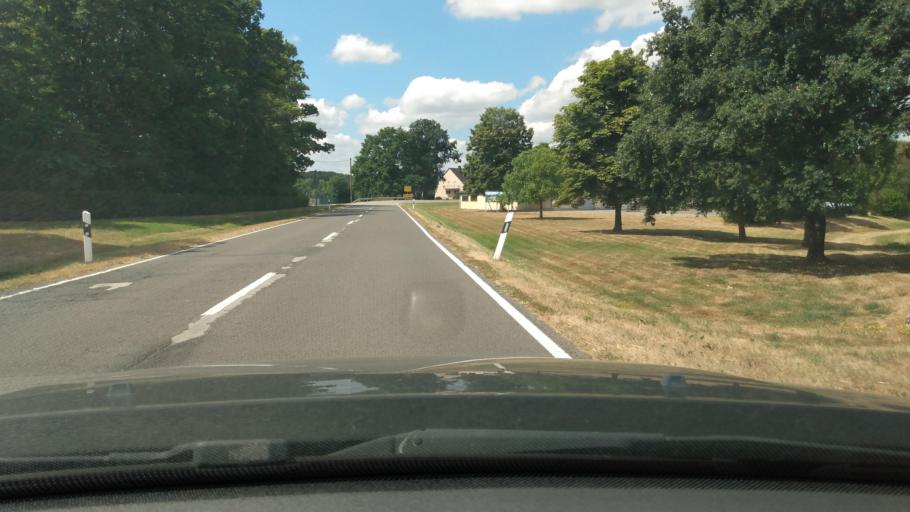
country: DE
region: Rheinland-Pfalz
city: Monzelfeld
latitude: 49.8887
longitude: 7.0783
